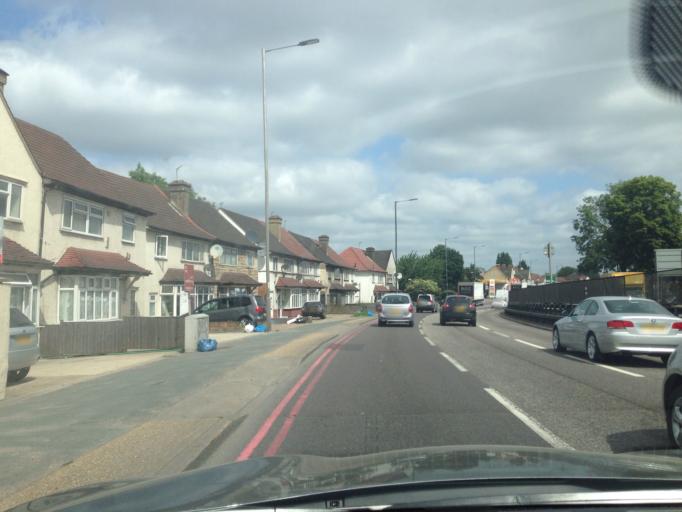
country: GB
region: England
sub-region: Greater London
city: Wembley
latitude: 51.5562
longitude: -0.2530
